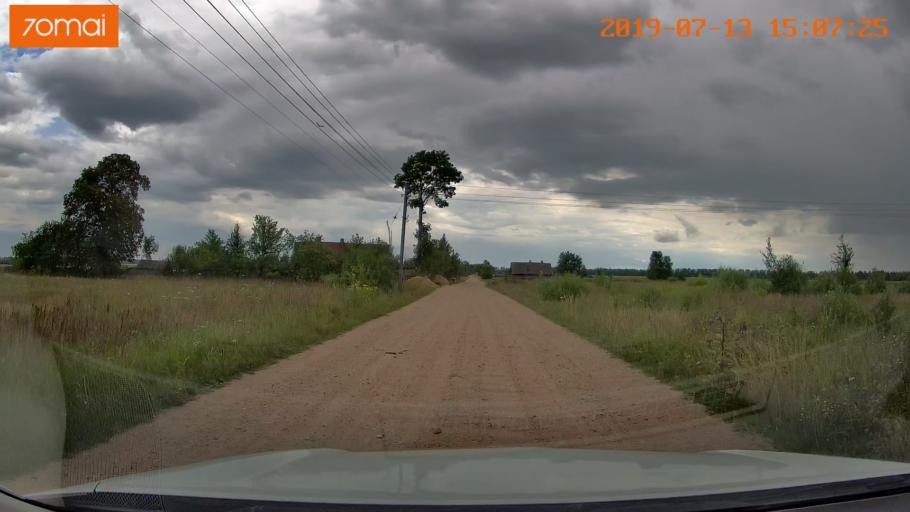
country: BY
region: Mogilev
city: Hlusha
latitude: 53.1907
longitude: 28.7568
